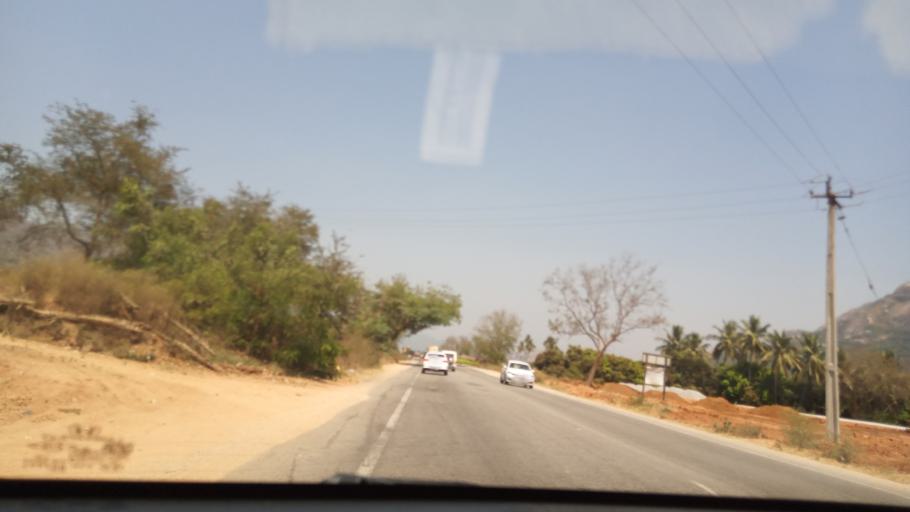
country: IN
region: Andhra Pradesh
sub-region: Chittoor
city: Narasingapuram
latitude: 13.5521
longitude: 79.2395
